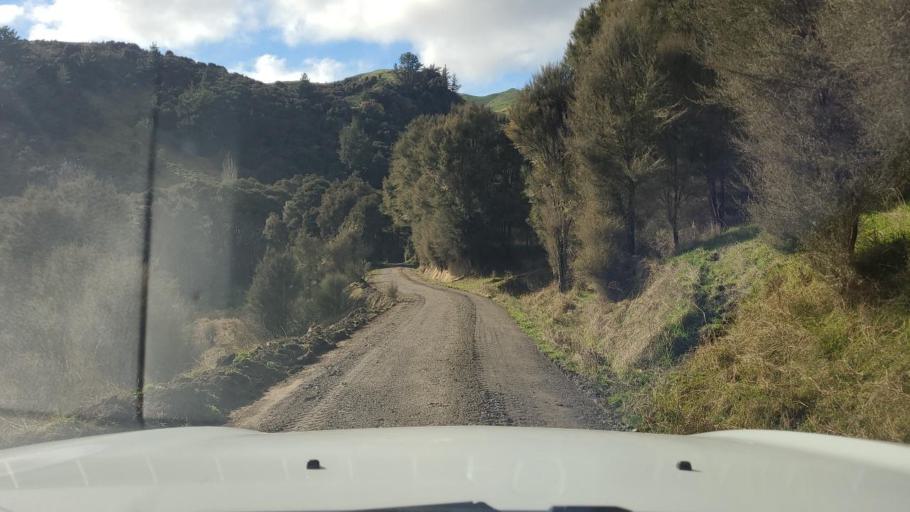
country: NZ
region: Wellington
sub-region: South Wairarapa District
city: Waipawa
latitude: -41.2348
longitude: 175.7068
